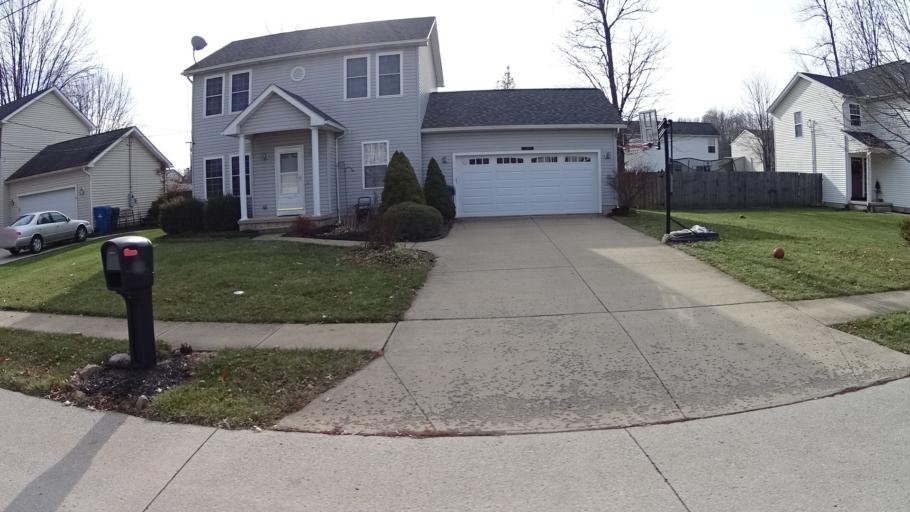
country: US
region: Ohio
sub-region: Lorain County
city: North Ridgeville
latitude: 41.3954
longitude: -81.9912
